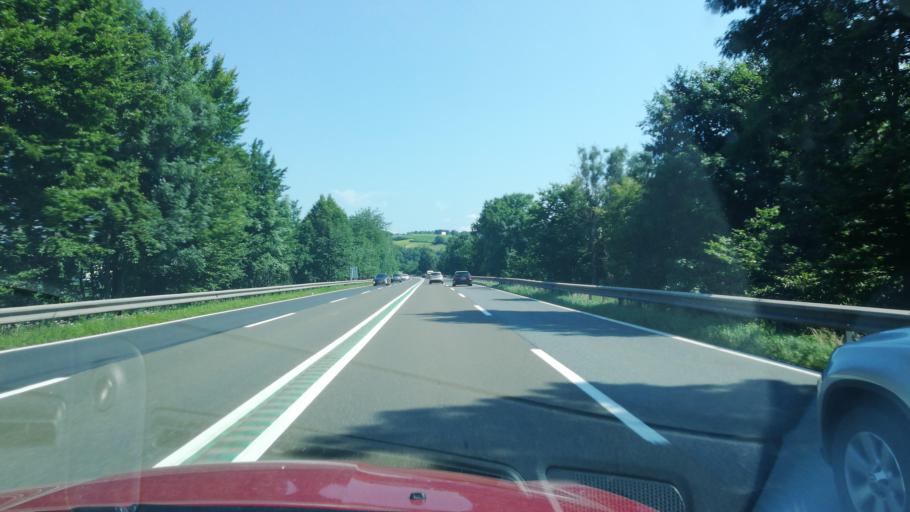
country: AT
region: Carinthia
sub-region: Politischer Bezirk Sankt Veit an der Glan
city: Sankt Veit an der Glan
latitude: 46.7341
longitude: 14.3834
